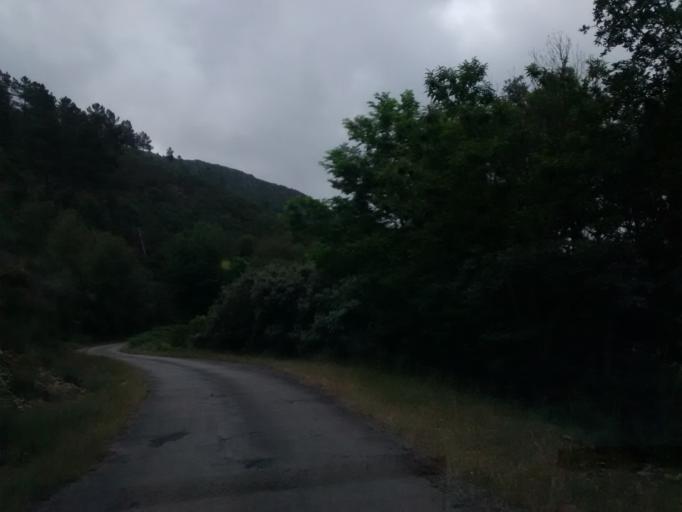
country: ES
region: Galicia
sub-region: Provincia de Ourense
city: Castro Caldelas
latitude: 42.4237
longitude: -7.3865
